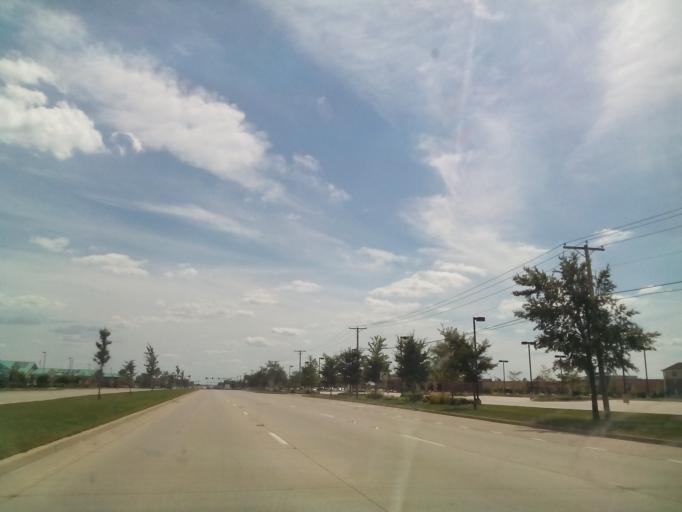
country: US
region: Illinois
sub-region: Will County
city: Plainfield
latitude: 41.7163
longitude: -88.2061
